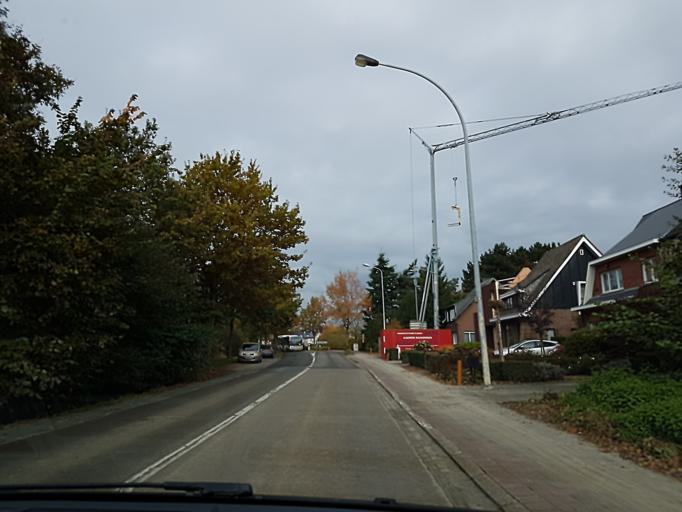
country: BE
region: Flanders
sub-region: Provincie Antwerpen
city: Boechout
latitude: 51.1493
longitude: 4.4835
